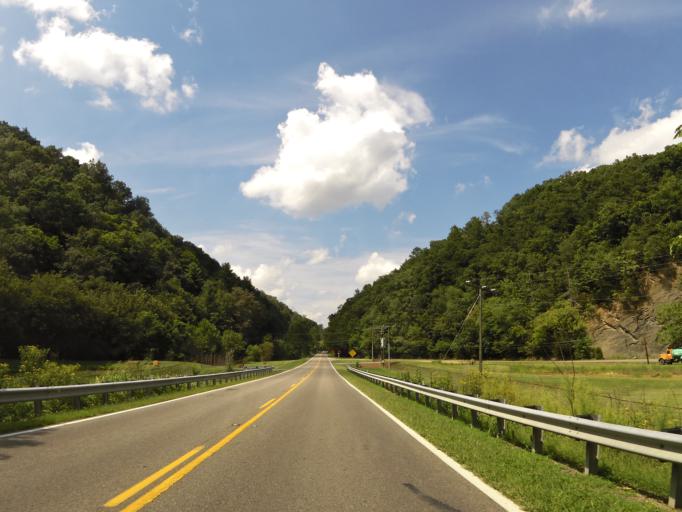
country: US
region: Virginia
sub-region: Washington County
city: Abingdon
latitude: 36.6697
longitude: -81.9687
